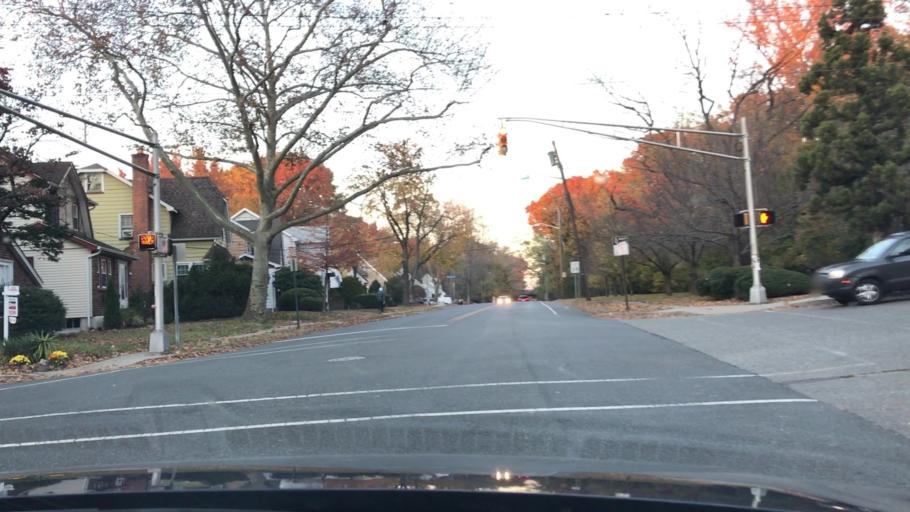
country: US
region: New Jersey
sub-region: Bergen County
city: Teaneck
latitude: 40.8923
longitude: -74.0168
